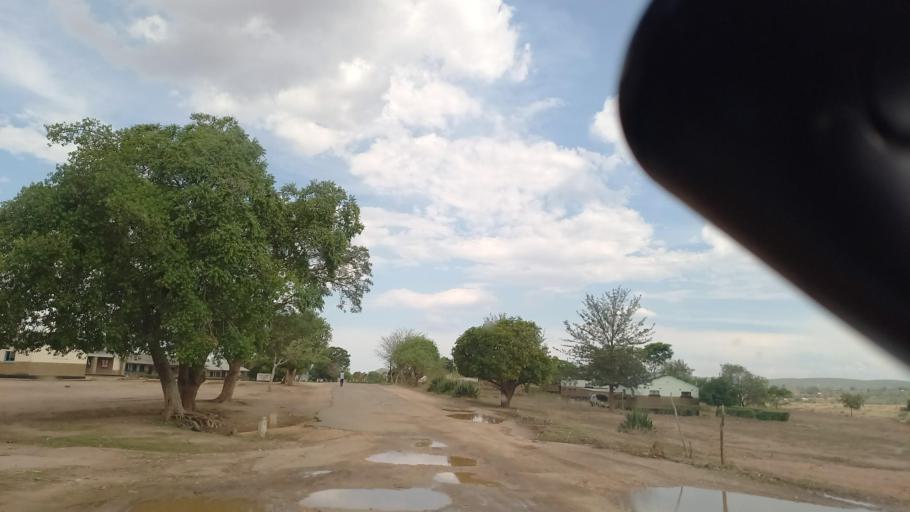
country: ZM
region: Lusaka
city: Kafue
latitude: -16.2252
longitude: 28.1320
